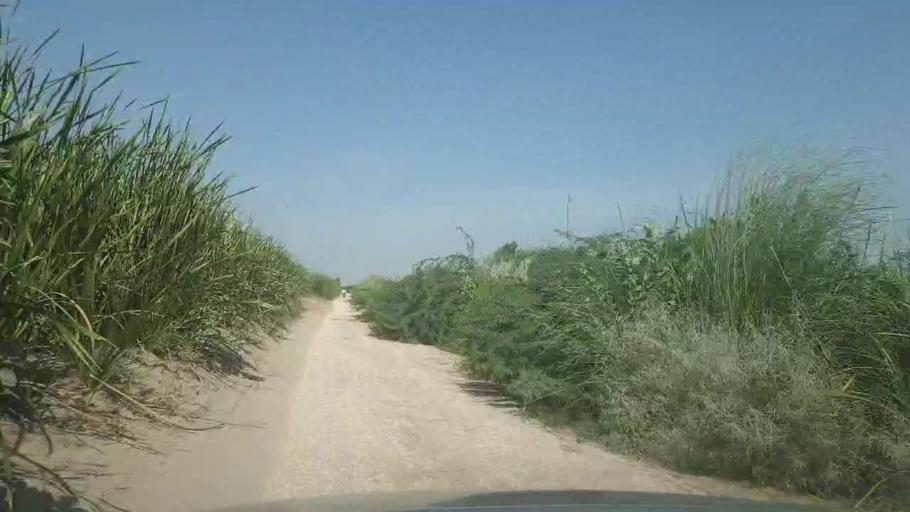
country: PK
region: Sindh
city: Khairpur
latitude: 27.3986
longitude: 69.0614
